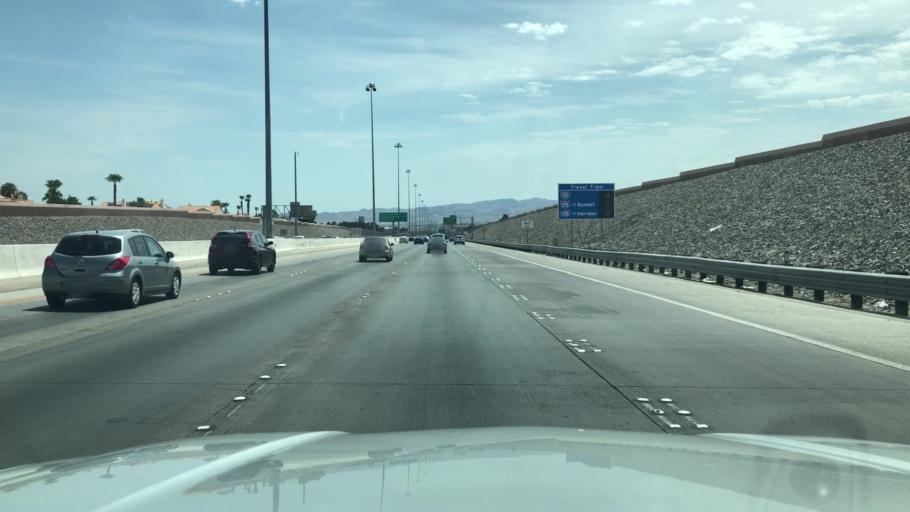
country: US
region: Nevada
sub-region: Clark County
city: Whitney
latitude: 36.0255
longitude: -115.0766
